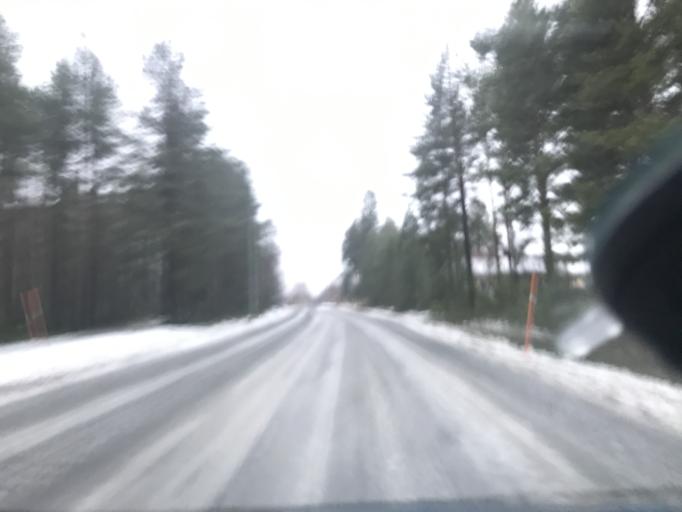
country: SE
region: Norrbotten
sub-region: Lulea Kommun
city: Sodra Sunderbyn
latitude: 65.6518
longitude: 21.9531
